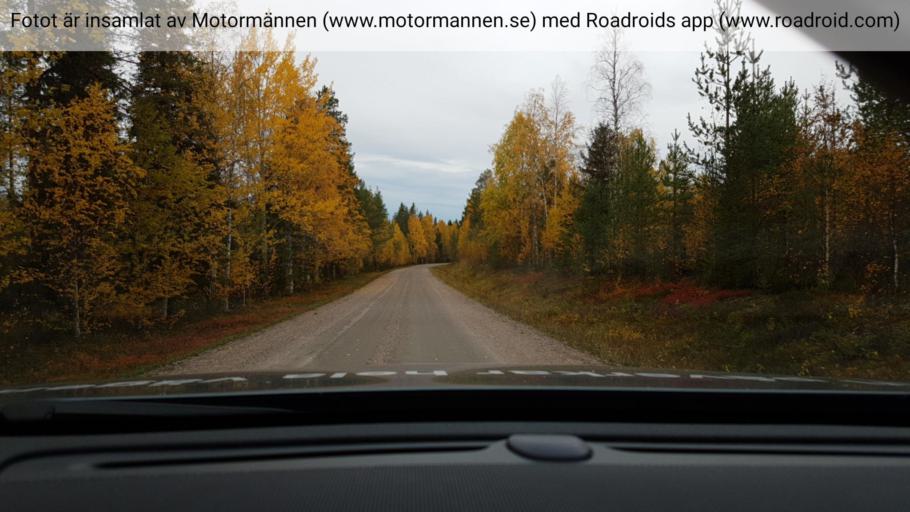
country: SE
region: Norrbotten
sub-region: Overkalix Kommun
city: OEverkalix
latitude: 66.2725
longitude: 22.9925
